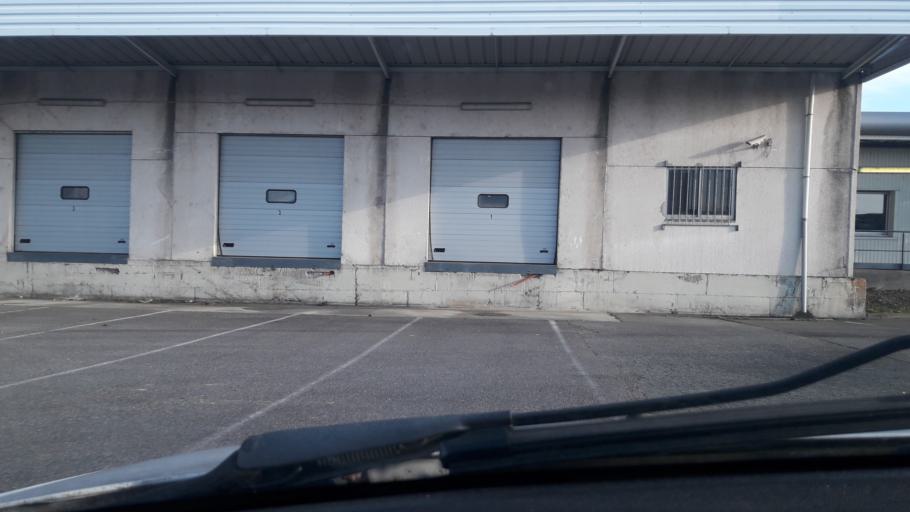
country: FR
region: Midi-Pyrenees
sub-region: Departement de la Haute-Garonne
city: Portet-sur-Garonne
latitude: 43.5543
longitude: 1.4153
